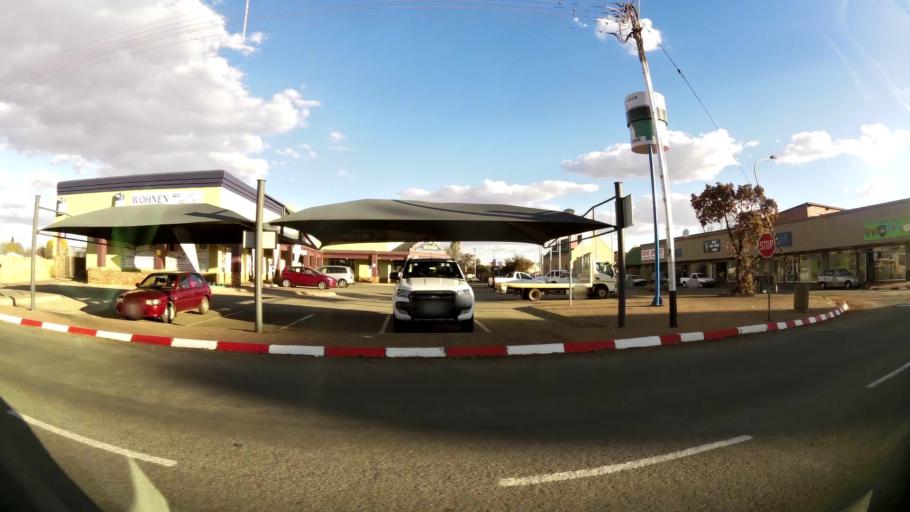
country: ZA
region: North-West
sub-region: Dr Kenneth Kaunda District Municipality
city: Potchefstroom
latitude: -26.7165
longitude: 27.0991
